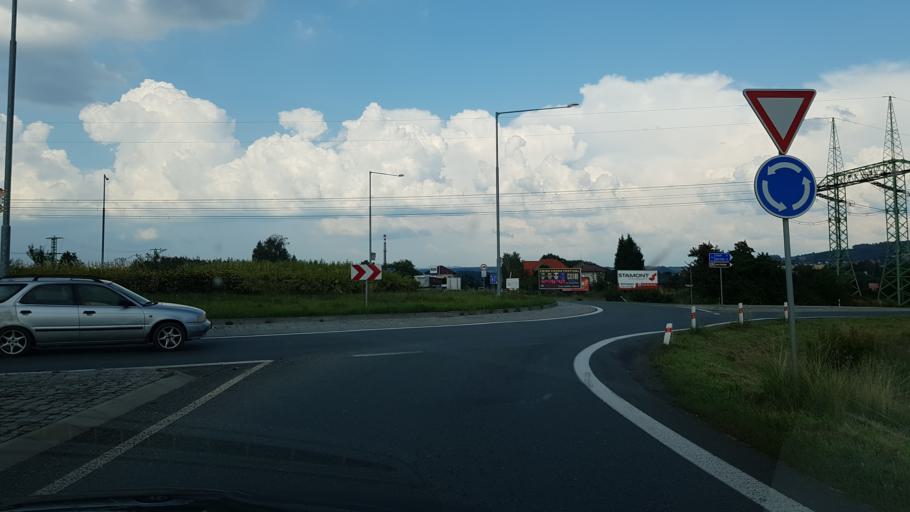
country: CZ
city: Doudleby nad Orlici
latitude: 50.1126
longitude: 16.2738
